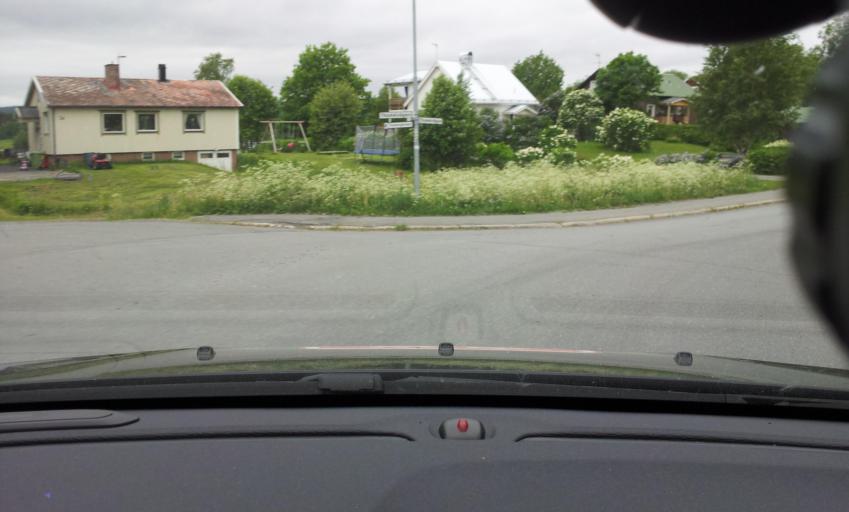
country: SE
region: Jaemtland
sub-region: Are Kommun
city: Jarpen
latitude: 63.3072
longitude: 13.6626
